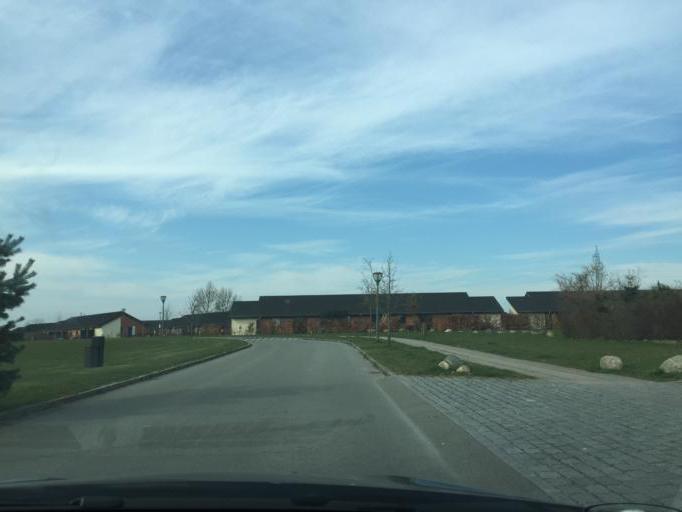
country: DK
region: South Denmark
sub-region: Odense Kommune
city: Neder Holluf
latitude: 55.3571
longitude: 10.5101
